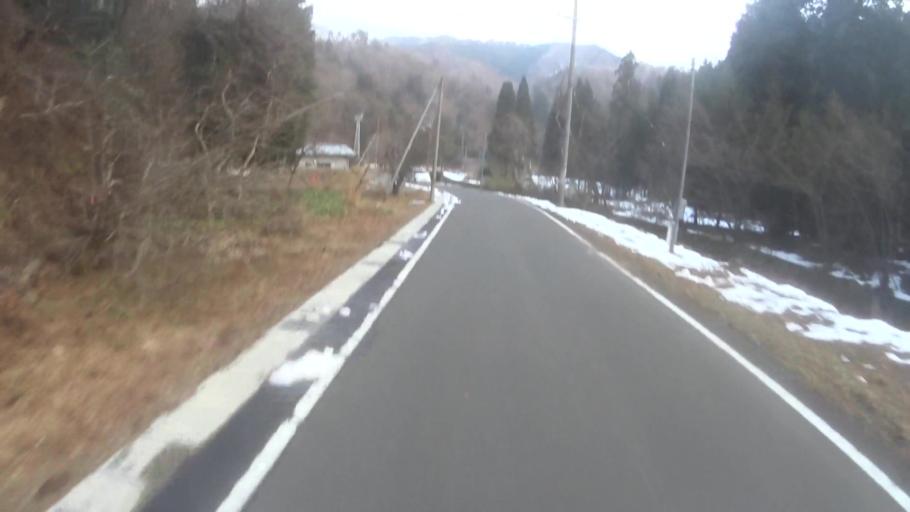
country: JP
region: Kyoto
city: Maizuru
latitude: 35.4327
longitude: 135.4769
